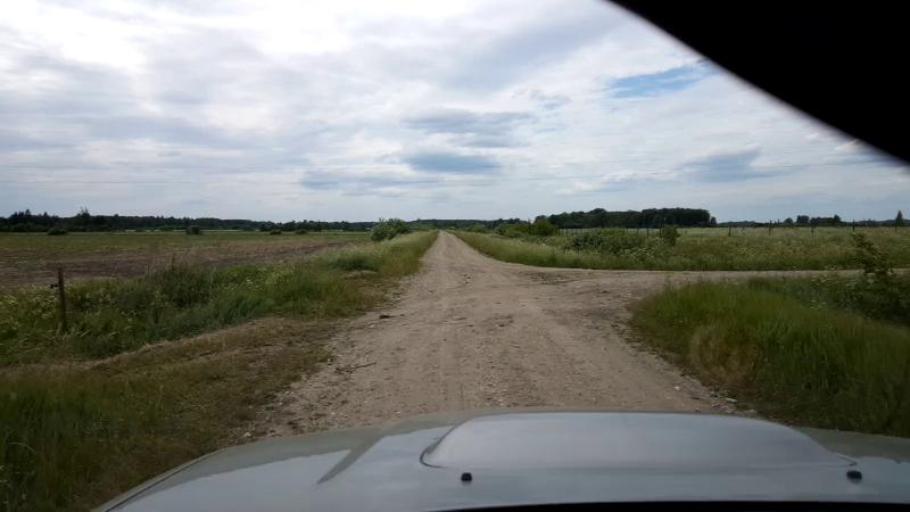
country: EE
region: Paernumaa
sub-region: Sauga vald
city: Sauga
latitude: 58.4923
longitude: 24.5820
